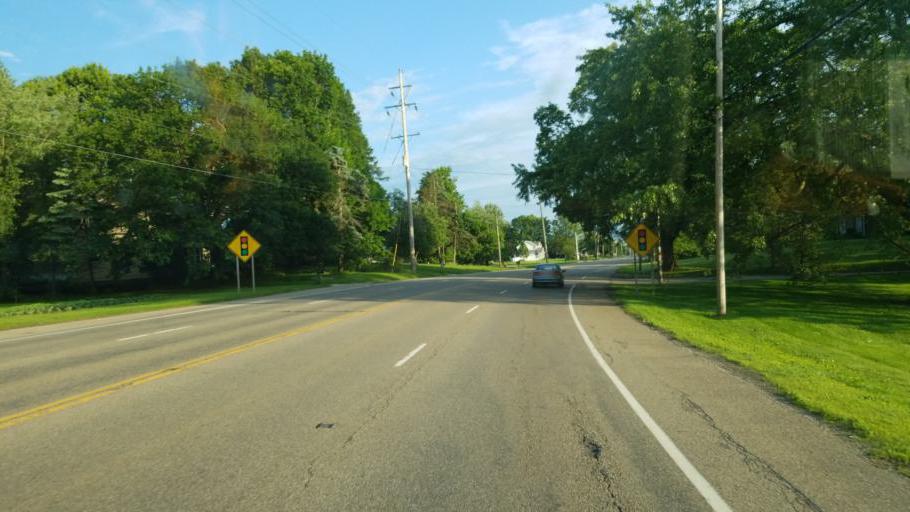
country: US
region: Ohio
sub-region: Stark County
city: Uniontown
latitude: 40.9987
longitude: -81.4058
